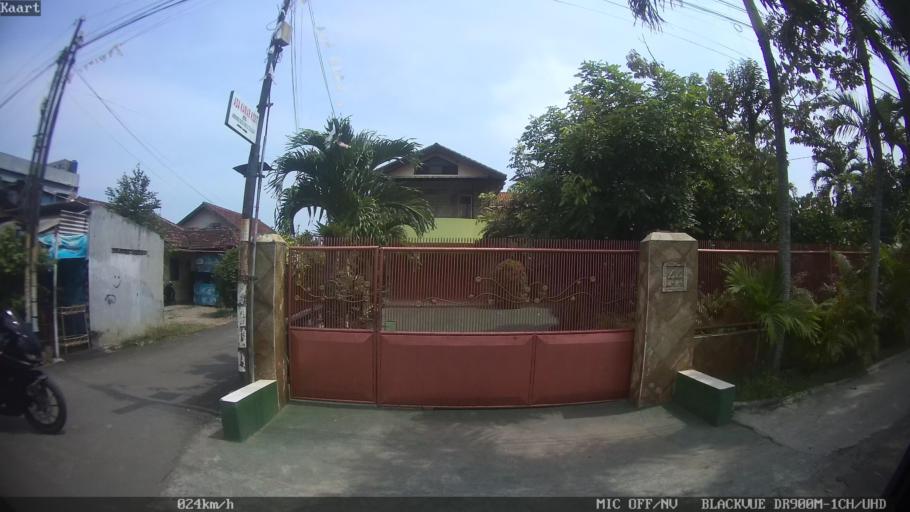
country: ID
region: Lampung
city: Bandarlampung
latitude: -5.4342
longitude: 105.2662
